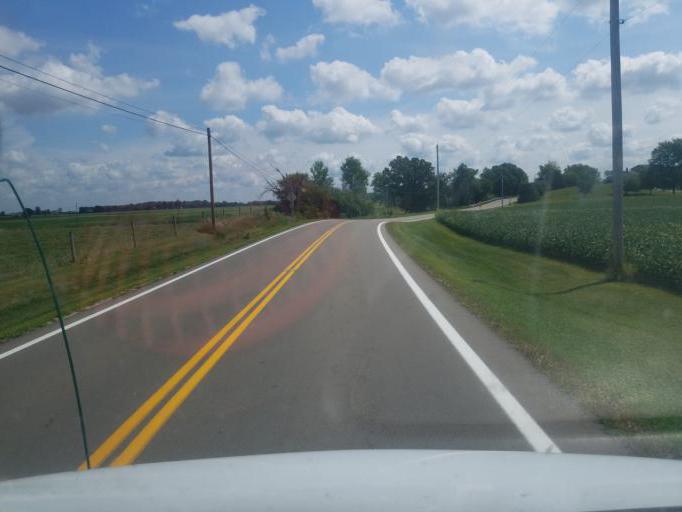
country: US
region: Ohio
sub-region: Marion County
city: Prospect
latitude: 40.3944
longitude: -83.1590
